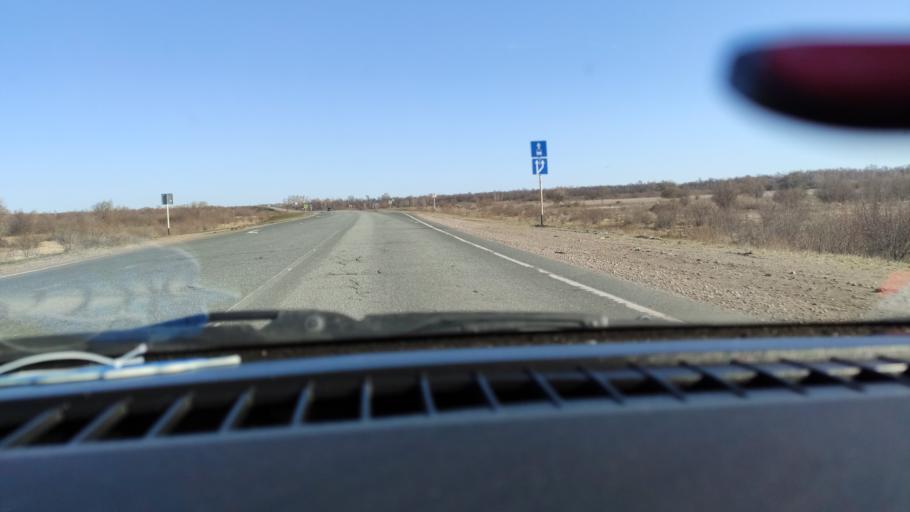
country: RU
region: Samara
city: Varlamovo
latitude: 53.1557
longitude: 48.2842
